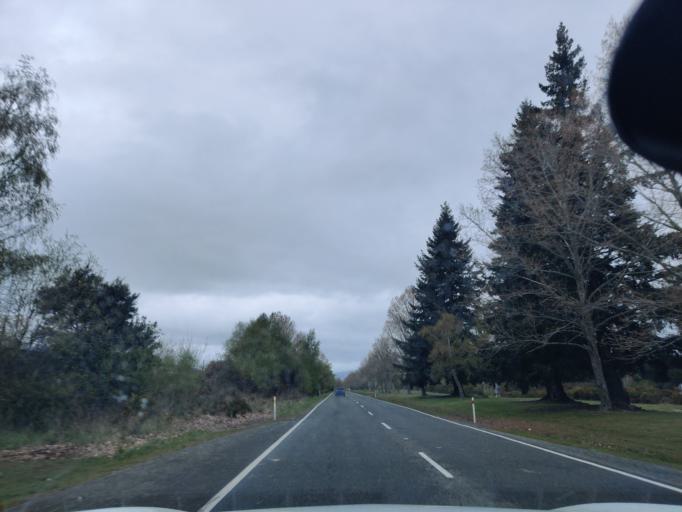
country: NZ
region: Waikato
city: Turangi
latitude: -38.9907
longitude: 175.7941
